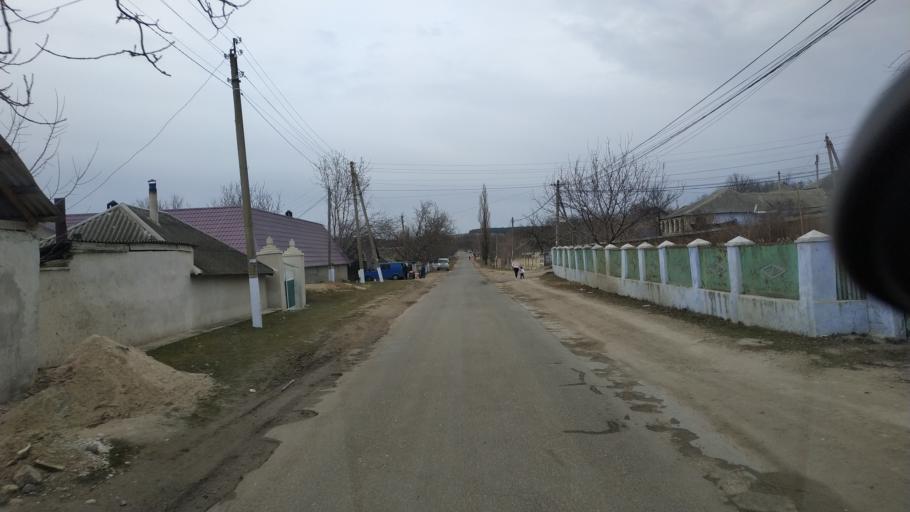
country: MD
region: Telenesti
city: Cocieri
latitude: 47.2688
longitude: 29.0667
